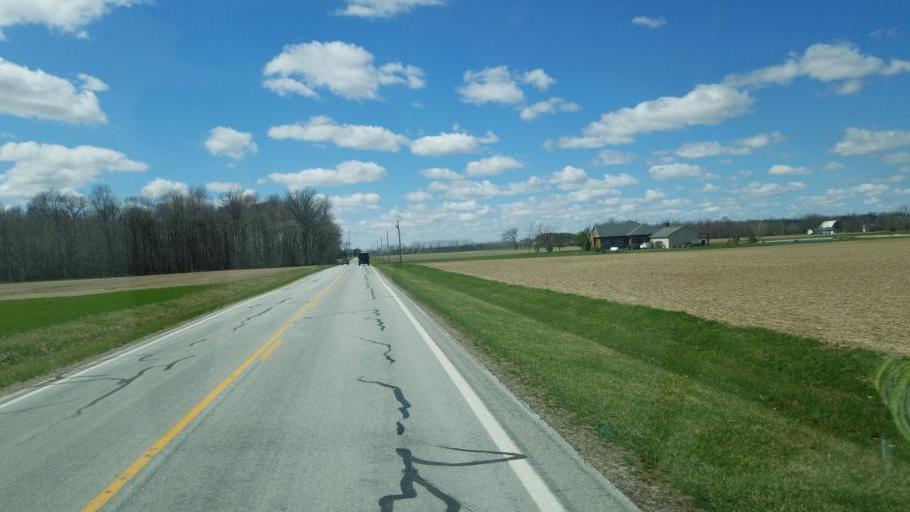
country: US
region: Ohio
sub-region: Hancock County
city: Arlington
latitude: 40.9201
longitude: -83.5391
